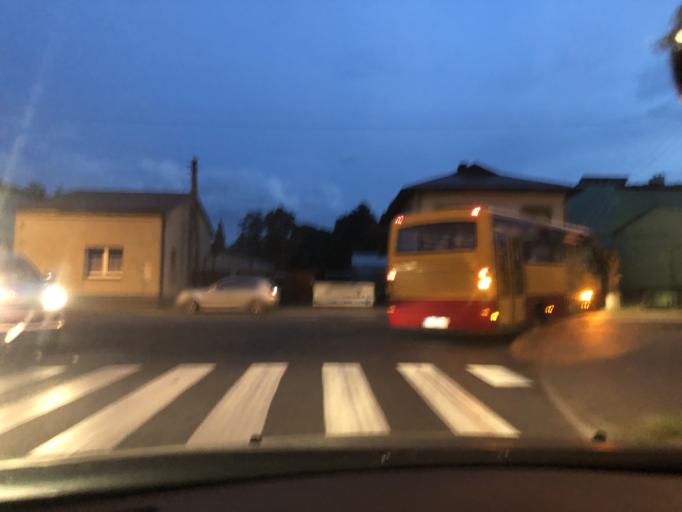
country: PL
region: Lodz Voivodeship
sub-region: Powiat wielunski
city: Wielun
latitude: 51.2218
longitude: 18.5580
